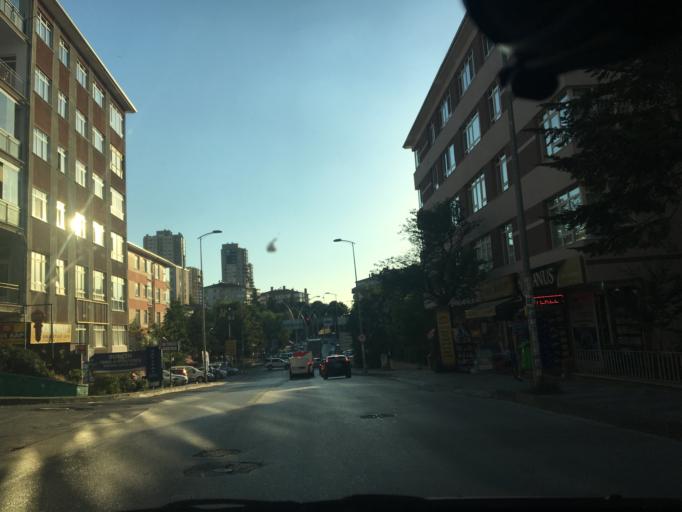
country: TR
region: Ankara
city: Ankara
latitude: 39.8954
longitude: 32.8510
